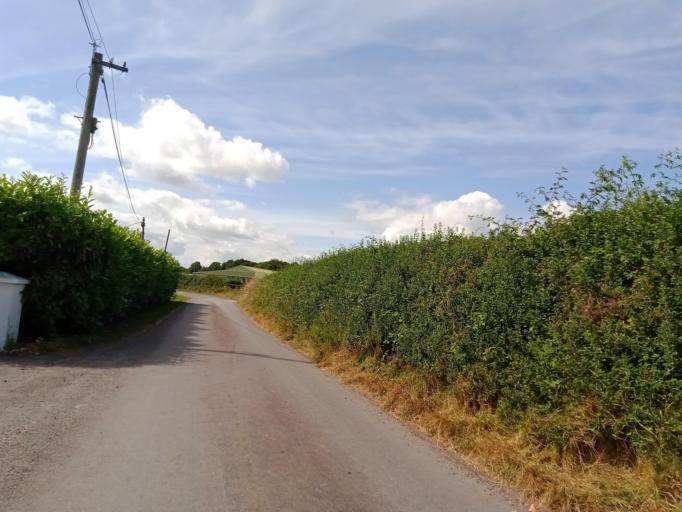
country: IE
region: Leinster
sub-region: Kilkenny
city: Kilkenny
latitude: 52.6365
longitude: -7.2100
